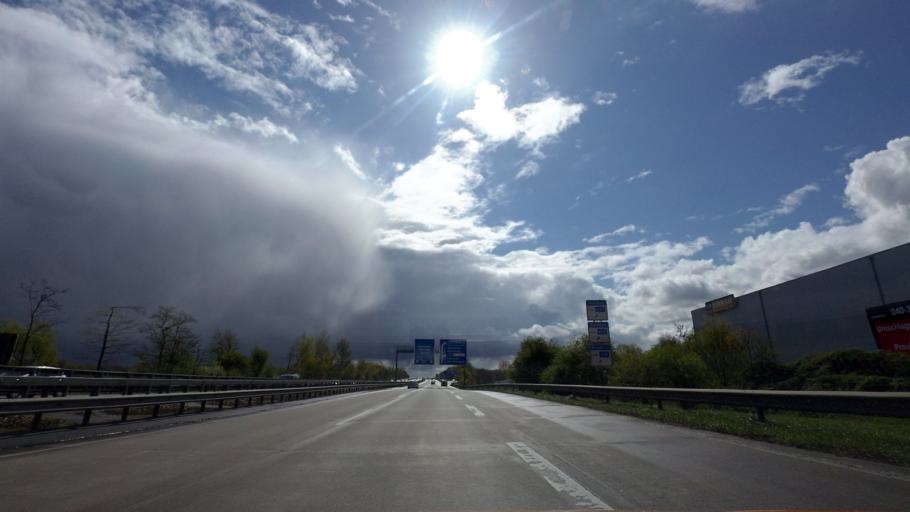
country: DE
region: Lower Saxony
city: Oyten
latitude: 53.0469
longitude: 8.9756
